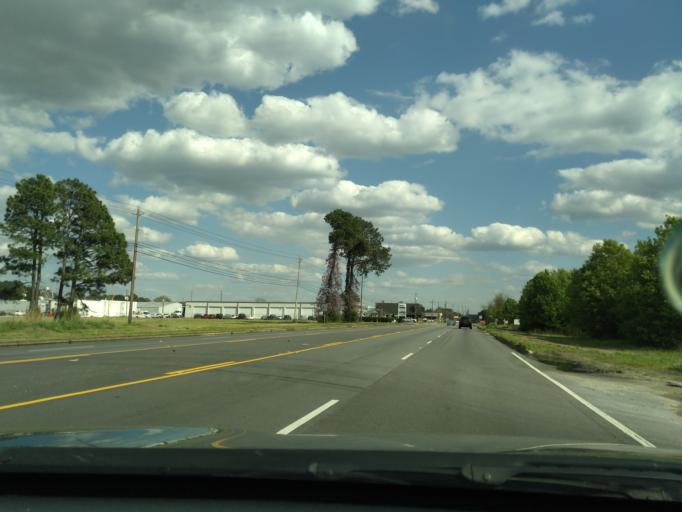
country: US
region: South Carolina
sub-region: Florence County
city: Florence
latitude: 34.2143
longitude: -79.7803
